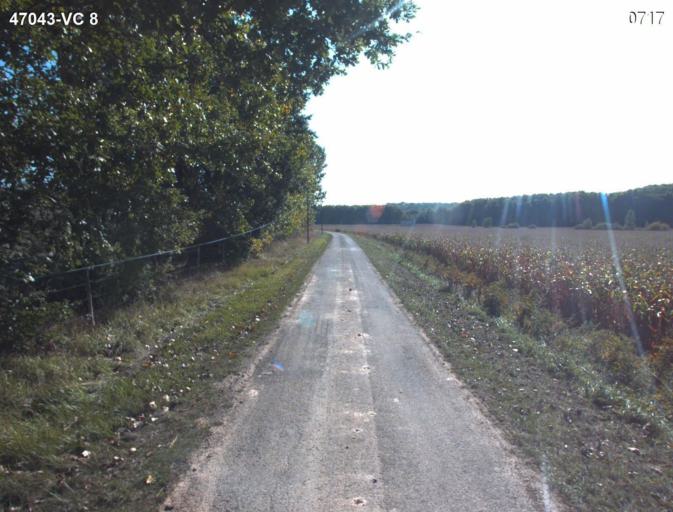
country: FR
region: Aquitaine
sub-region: Departement du Lot-et-Garonne
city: Buzet-sur-Baise
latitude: 44.2755
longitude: 0.2910
